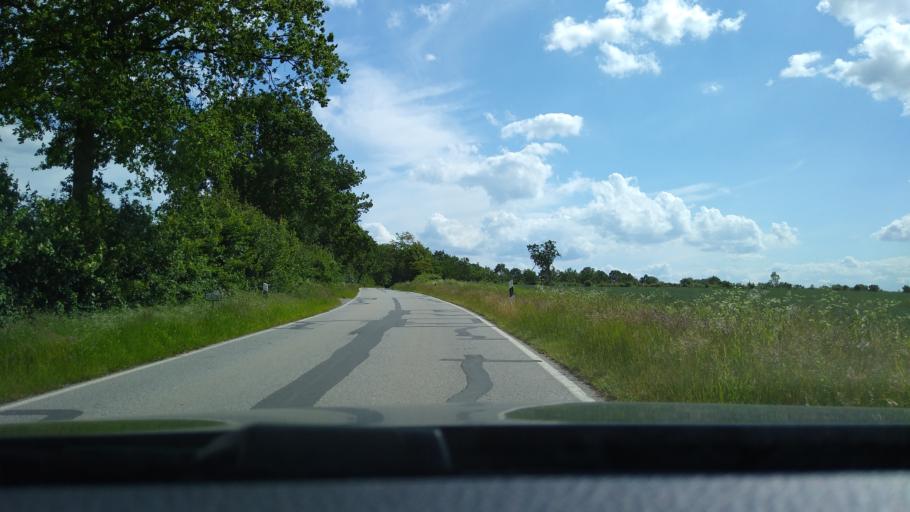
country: DE
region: Schleswig-Holstein
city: Kabelhorst
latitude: 54.2208
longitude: 10.9316
